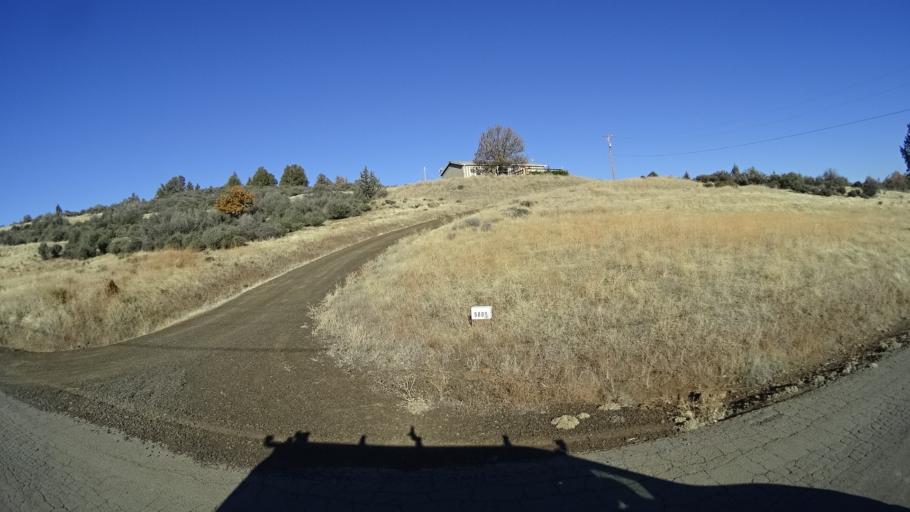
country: US
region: California
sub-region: Siskiyou County
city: Montague
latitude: 41.8804
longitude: -122.4567
